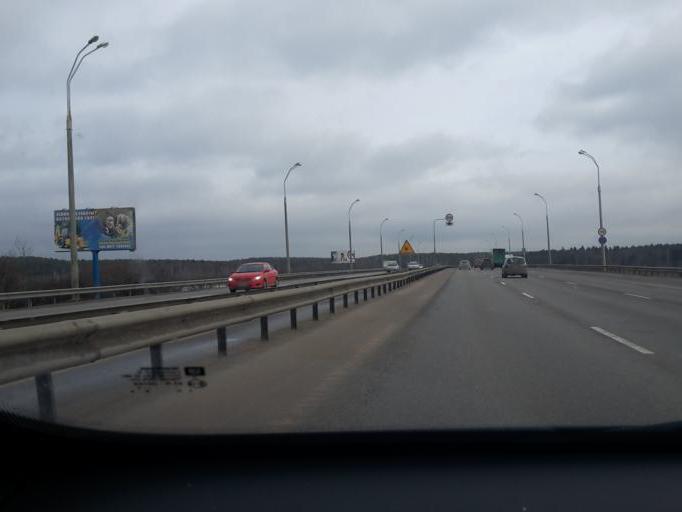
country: BY
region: Minsk
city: Zhdanovichy
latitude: 53.9558
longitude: 27.4521
